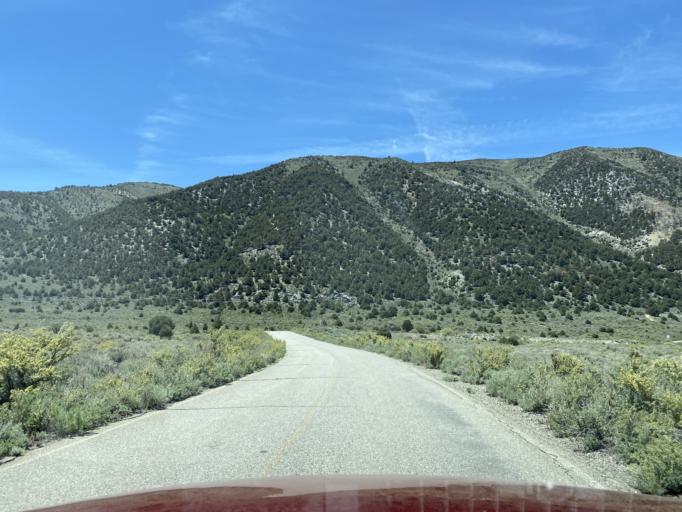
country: US
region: California
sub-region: Mono County
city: Bridgeport
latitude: 37.9645
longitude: -119.1228
